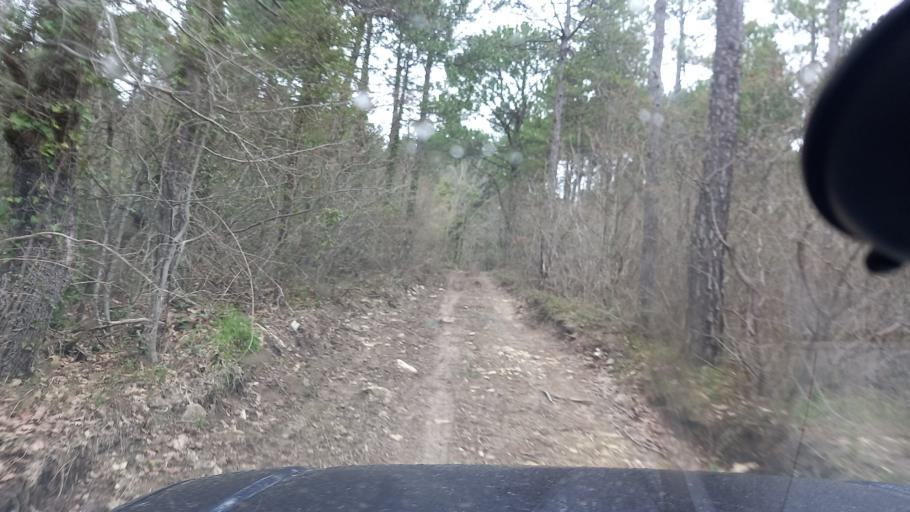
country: RU
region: Krasnodarskiy
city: Arkhipo-Osipovka
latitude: 44.3747
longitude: 38.4737
